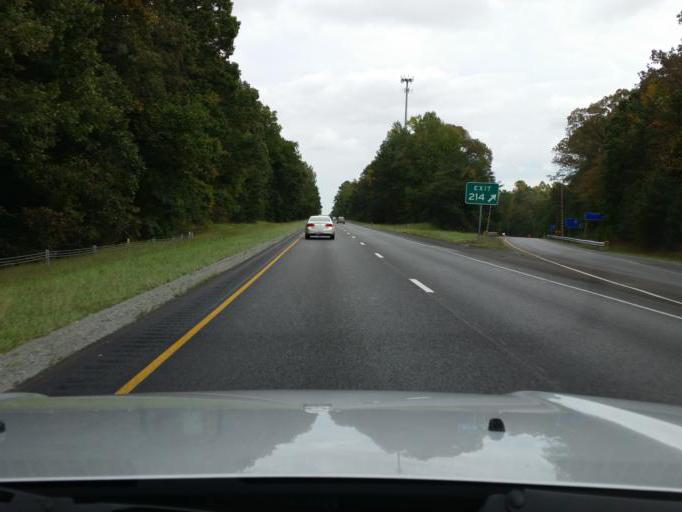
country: US
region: Virginia
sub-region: New Kent County
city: New Kent
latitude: 37.4957
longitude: -77.0283
